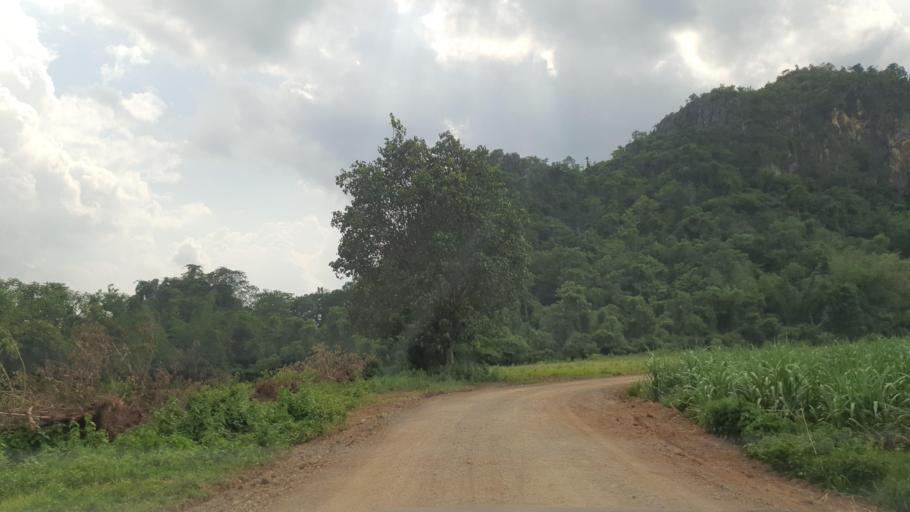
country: TH
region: Sukhothai
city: Thung Saliam
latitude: 17.2512
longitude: 99.5431
